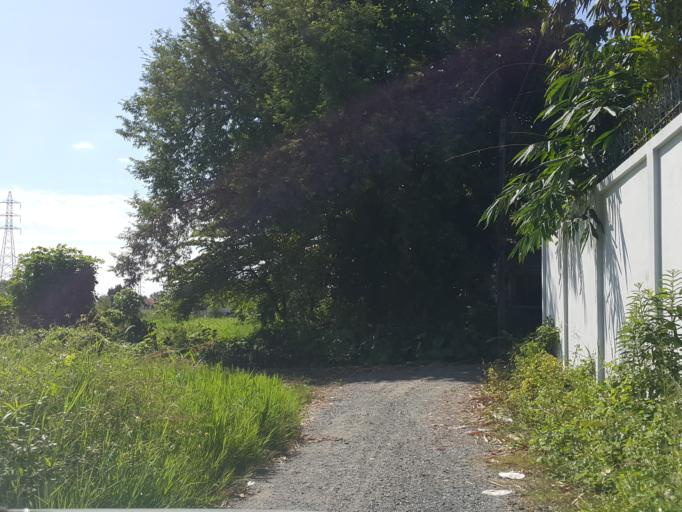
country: TH
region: Chiang Mai
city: San Sai
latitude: 18.8100
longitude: 99.0292
